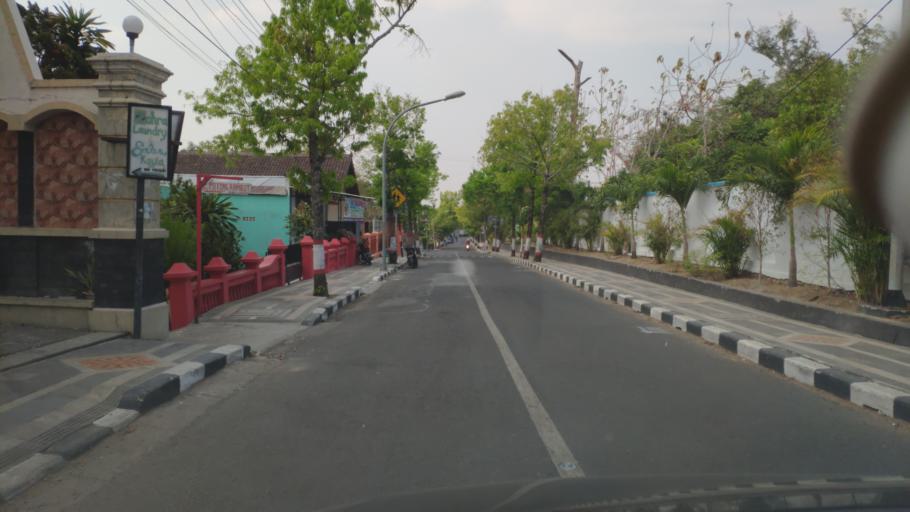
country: ID
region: Central Java
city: Tempelan
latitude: -6.9684
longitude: 111.4127
